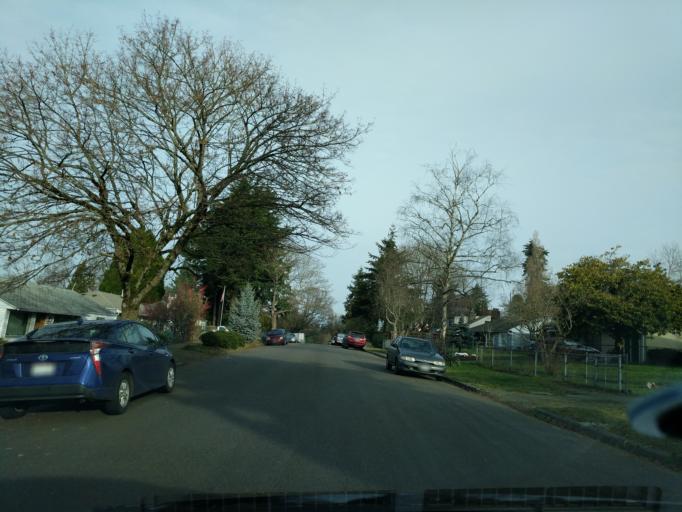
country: US
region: Washington
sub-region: King County
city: Shoreline
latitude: 47.7524
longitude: -122.3267
